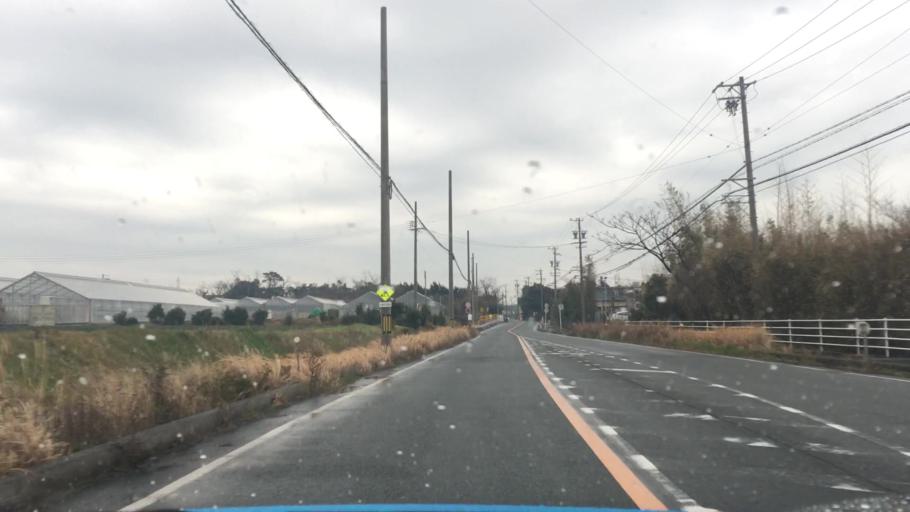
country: JP
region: Aichi
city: Toyohashi
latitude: 34.6896
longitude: 137.3904
